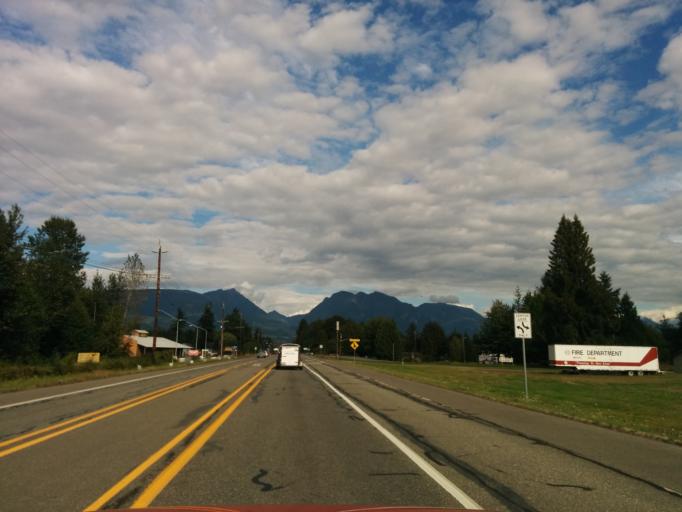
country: US
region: Washington
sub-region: Snohomish County
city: Sultan
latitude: 47.8662
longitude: -121.7912
